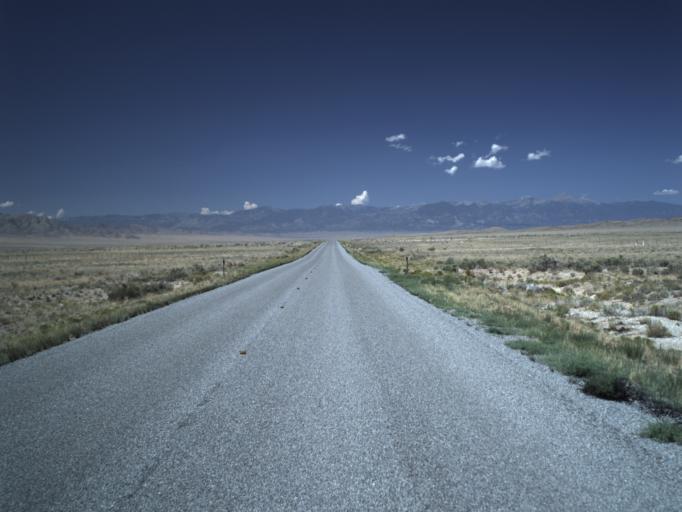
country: US
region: Utah
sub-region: Beaver County
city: Milford
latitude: 39.0681
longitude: -113.7343
